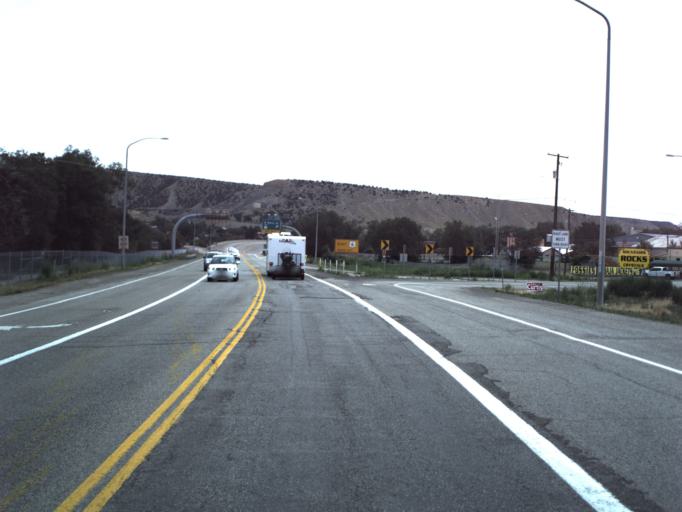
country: US
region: Utah
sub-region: Carbon County
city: Helper
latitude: 39.6941
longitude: -110.8638
